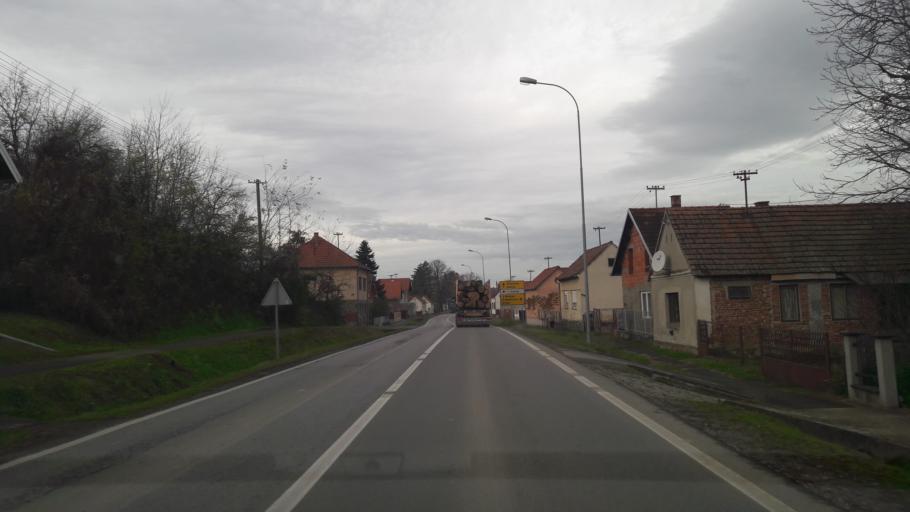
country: HR
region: Virovitick-Podravska
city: Orahovica
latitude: 45.5469
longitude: 17.9063
